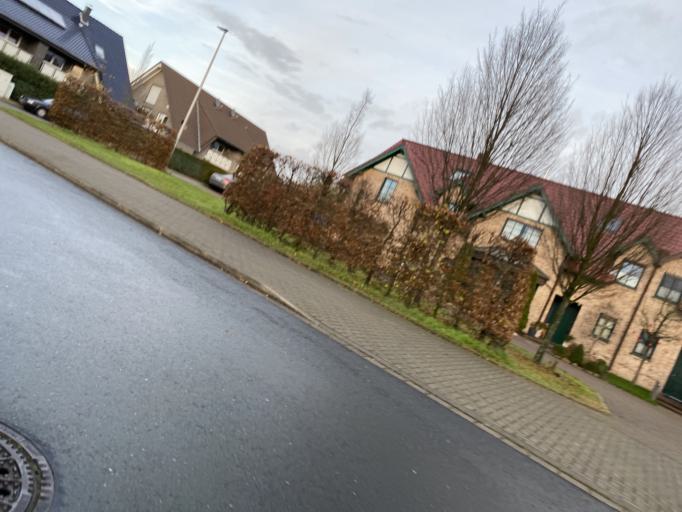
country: DE
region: North Rhine-Westphalia
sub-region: Regierungsbezirk Arnsberg
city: Hamm
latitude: 51.6828
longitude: 7.8661
